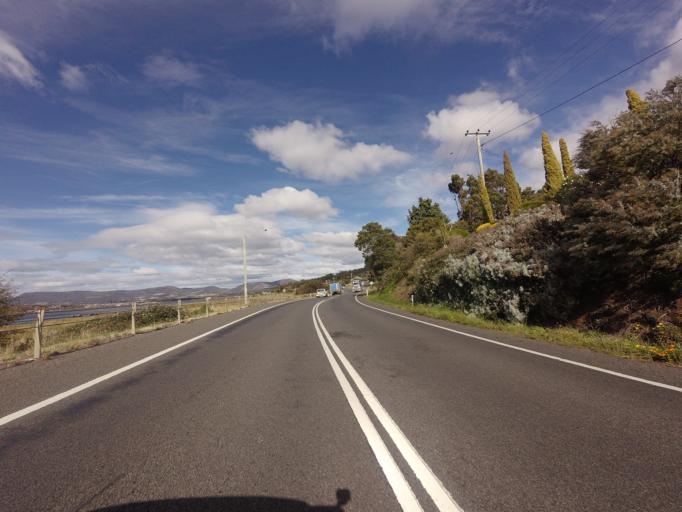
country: AU
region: Tasmania
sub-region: Brighton
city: Bridgewater
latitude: -42.7438
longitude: 147.2125
